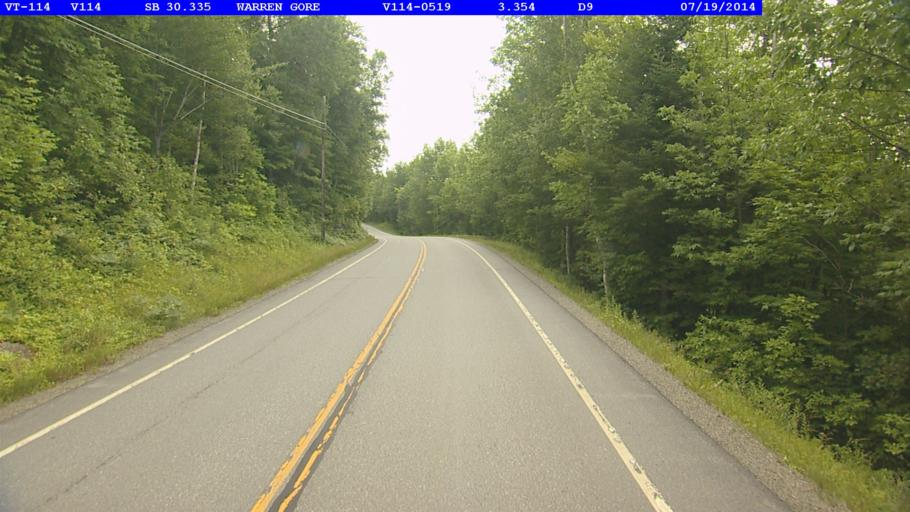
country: CA
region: Quebec
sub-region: Estrie
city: Coaticook
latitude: 44.9304
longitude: -71.8668
